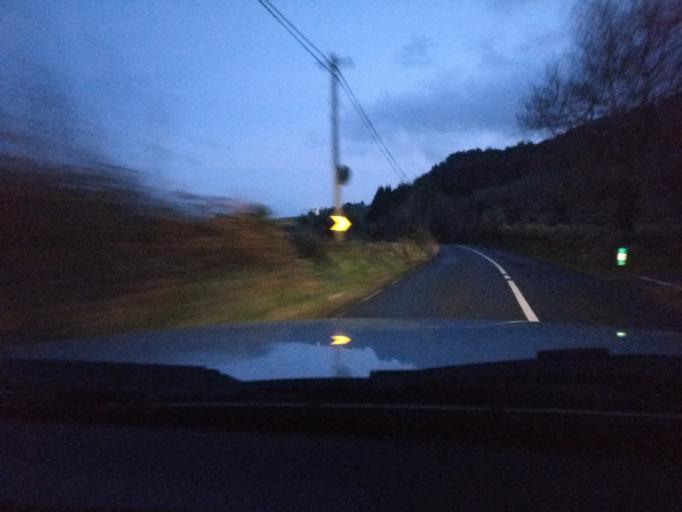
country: GB
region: Northern Ireland
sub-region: Down District
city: Warrenpoint
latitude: 54.0701
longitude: -6.2304
